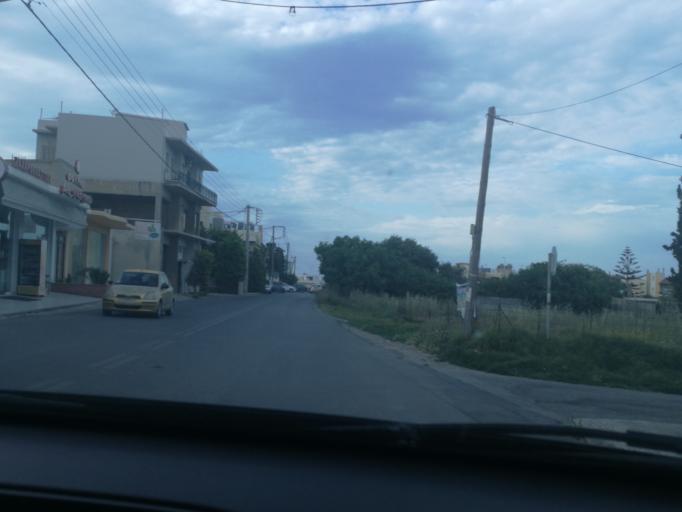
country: GR
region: Crete
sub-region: Nomos Irakleiou
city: Irakleion
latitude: 35.3123
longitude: 25.1397
